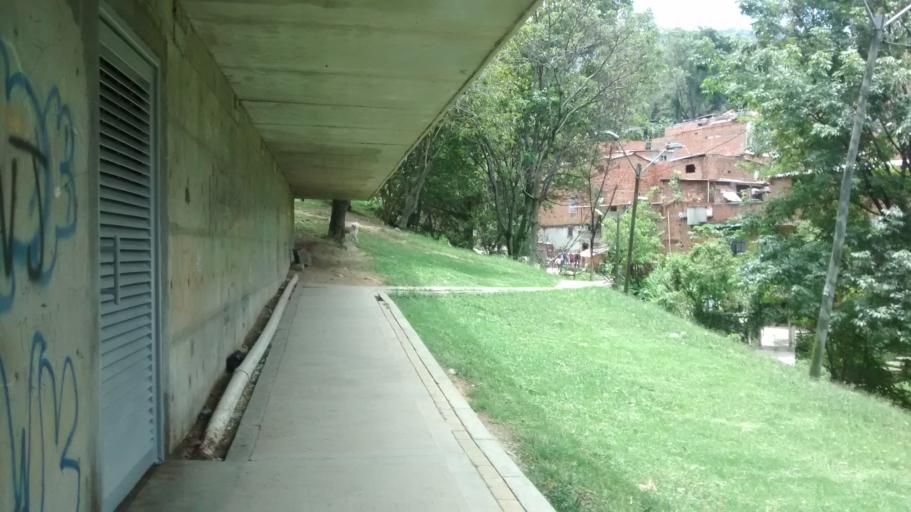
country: CO
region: Antioquia
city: Medellin
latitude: 6.2857
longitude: -75.5834
